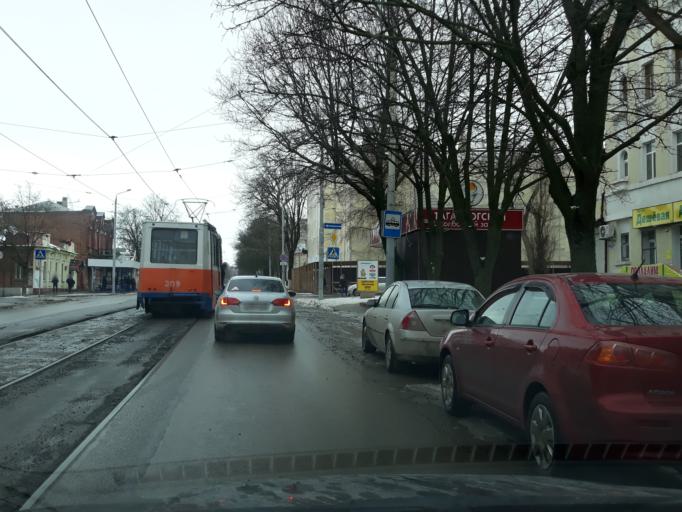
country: RU
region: Rostov
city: Taganrog
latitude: 47.2142
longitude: 38.9277
